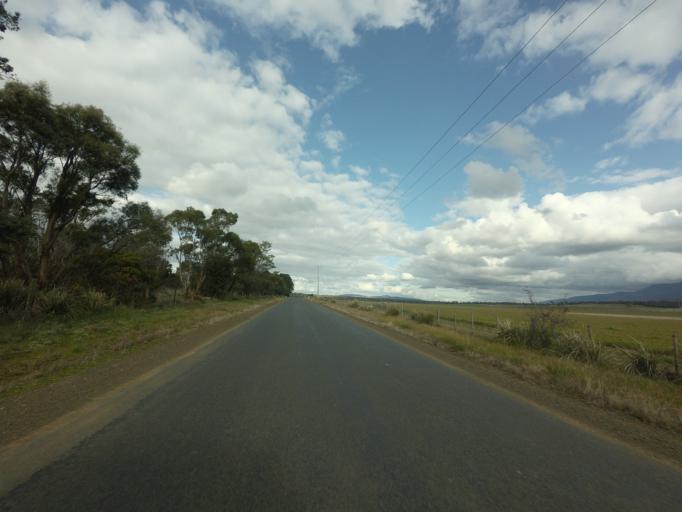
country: AU
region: Tasmania
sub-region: Northern Midlands
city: Longford
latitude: -41.8186
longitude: 147.1989
